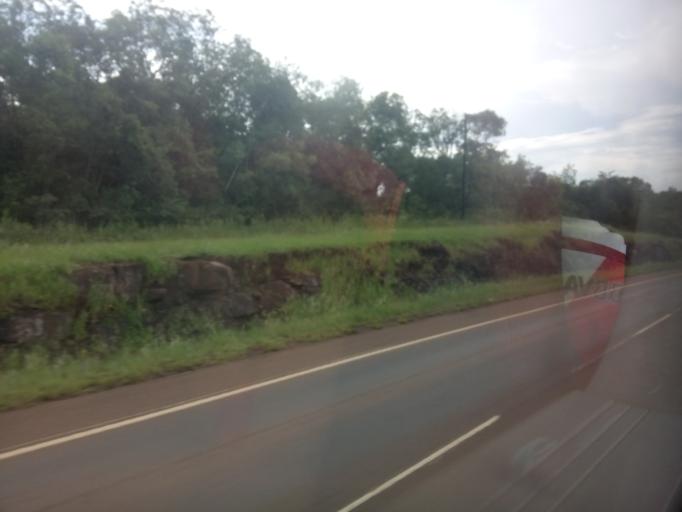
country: AR
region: Misiones
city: Santa Ana
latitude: -27.3997
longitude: -55.6025
